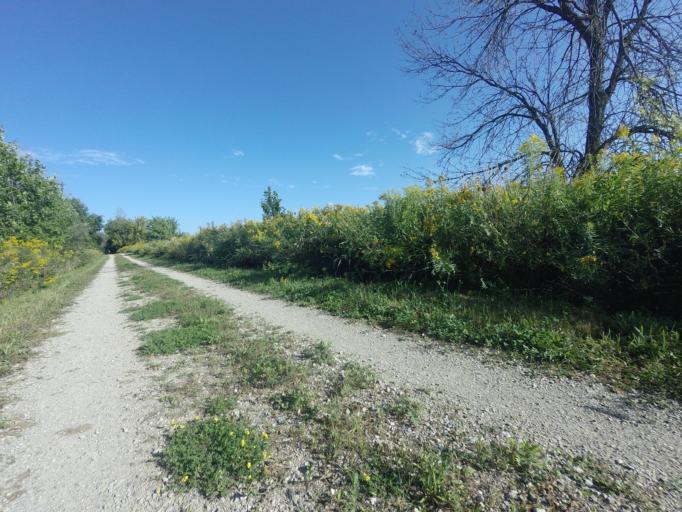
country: CA
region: Ontario
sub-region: Wellington County
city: Guelph
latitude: 43.6605
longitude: -80.4293
